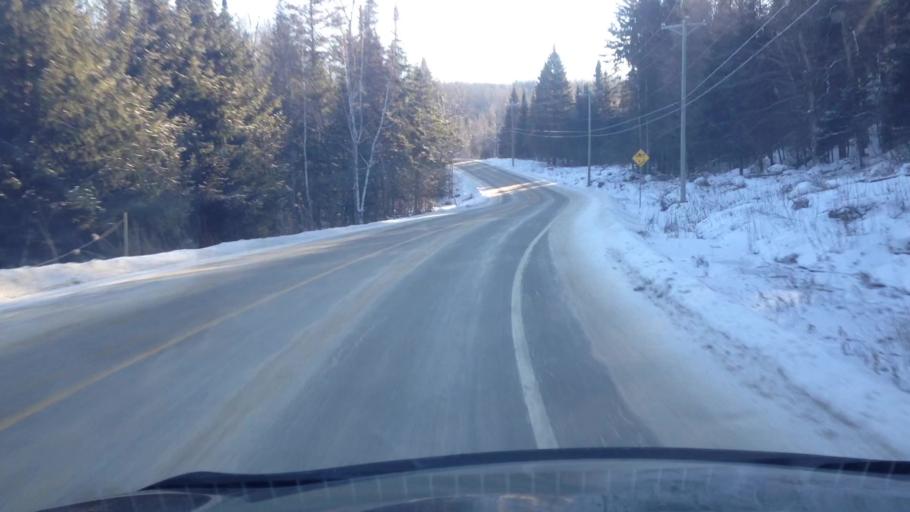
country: CA
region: Quebec
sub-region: Laurentides
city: Brownsburg-Chatham
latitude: 45.9211
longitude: -74.5262
